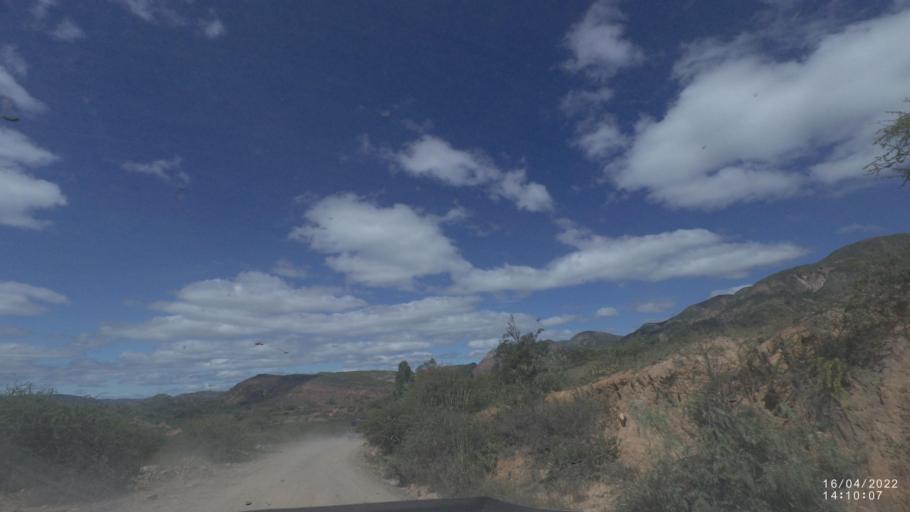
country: BO
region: Cochabamba
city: Mizque
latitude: -18.0619
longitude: -65.5210
